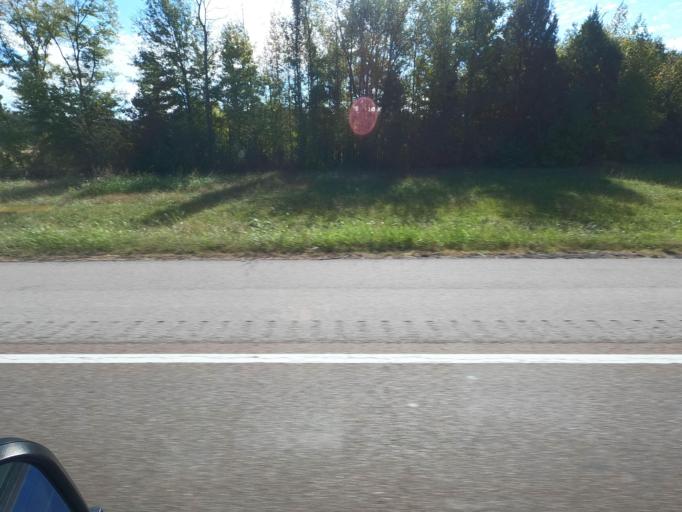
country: US
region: Tennessee
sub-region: Fayette County
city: Hickory Withe
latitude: 35.2935
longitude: -89.6078
